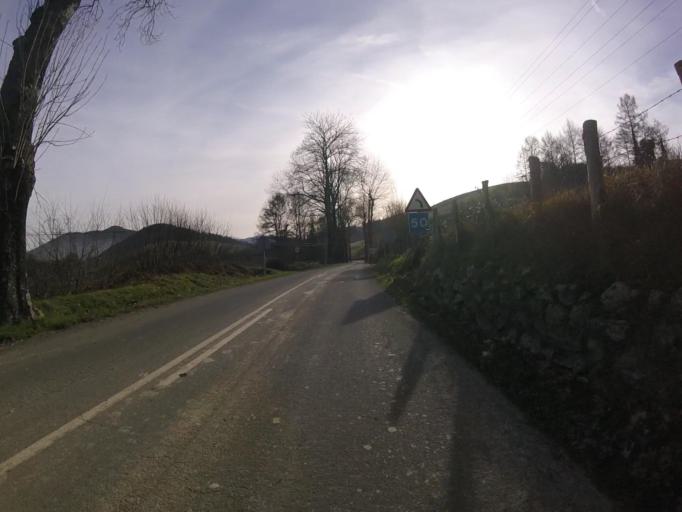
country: ES
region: Basque Country
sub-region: Provincia de Guipuzcoa
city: Berastegui
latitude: 43.1074
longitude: -1.9634
